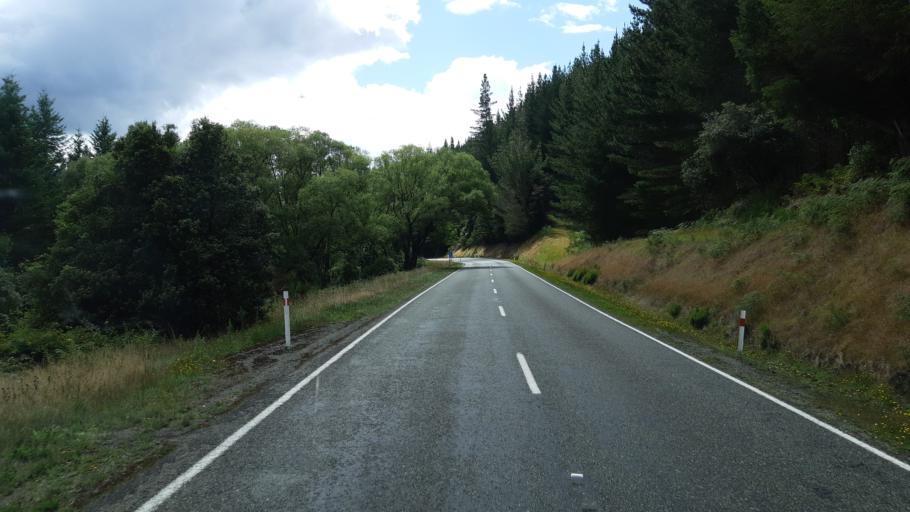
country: NZ
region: Tasman
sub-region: Tasman District
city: Wakefield
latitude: -41.5977
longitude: 172.7616
